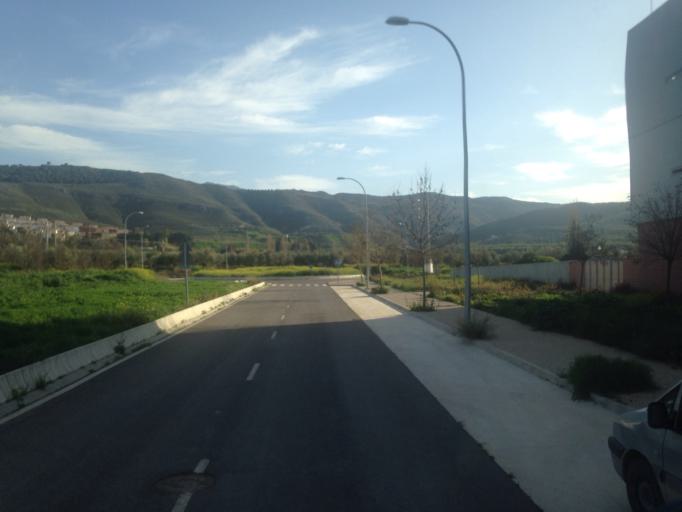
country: ES
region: Andalusia
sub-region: Provincia de Malaga
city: Antequera
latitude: 37.0243
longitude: -4.5793
